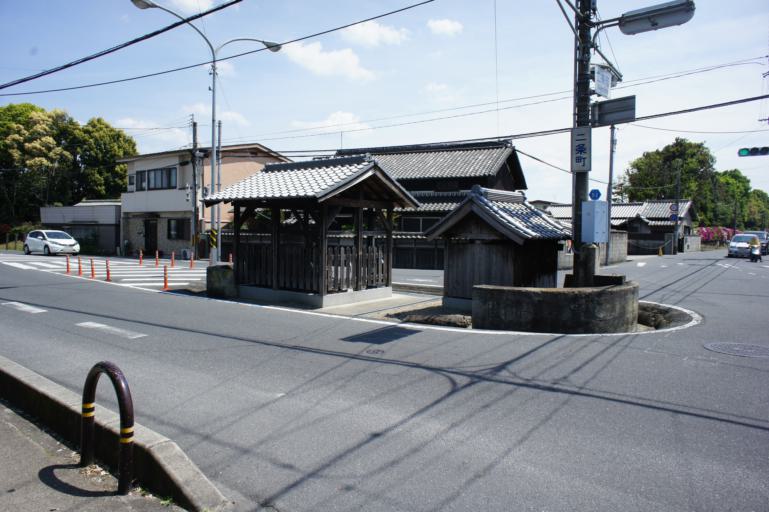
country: JP
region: Nara
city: Nara-shi
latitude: 34.6940
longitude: 135.7887
